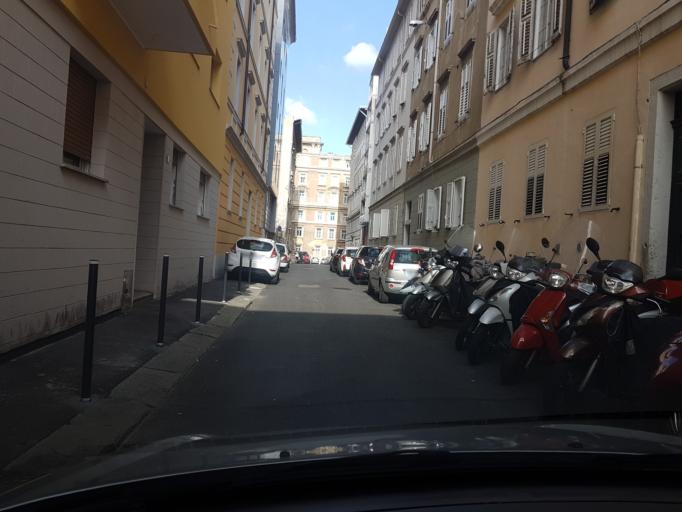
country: IT
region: Friuli Venezia Giulia
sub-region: Provincia di Trieste
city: Trieste
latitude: 45.6451
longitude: 13.7661
